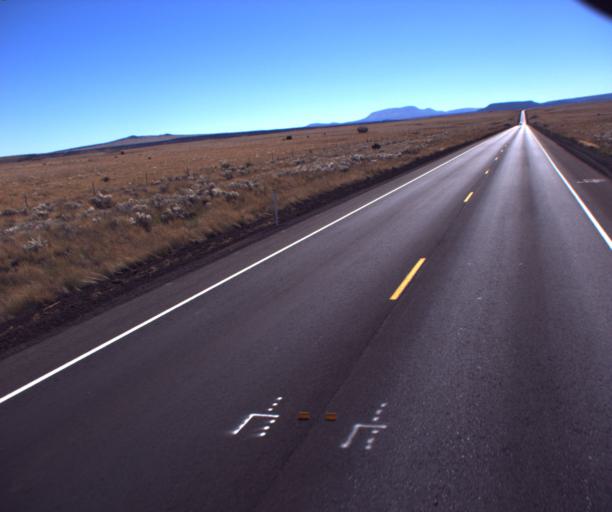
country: US
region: Arizona
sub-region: Apache County
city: Springerville
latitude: 34.2218
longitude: -109.3363
